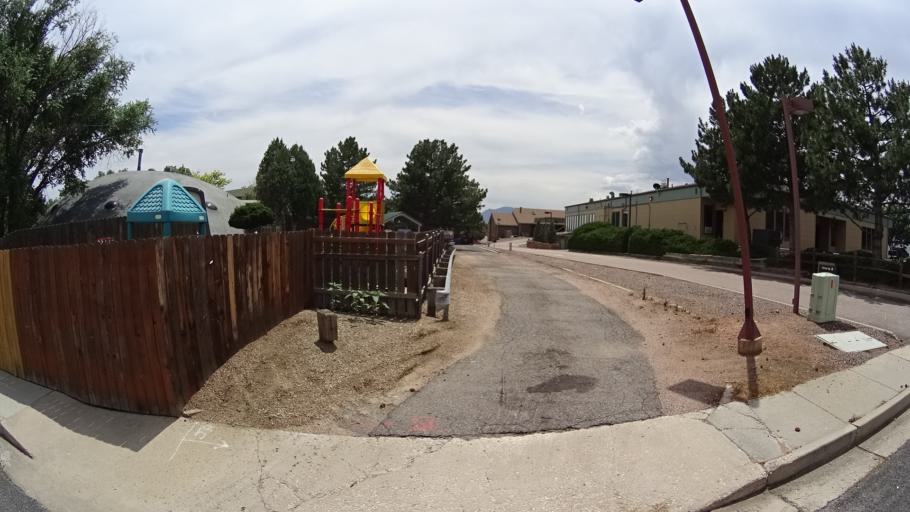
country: US
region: Colorado
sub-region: El Paso County
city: Colorado Springs
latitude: 38.8983
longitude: -104.8350
